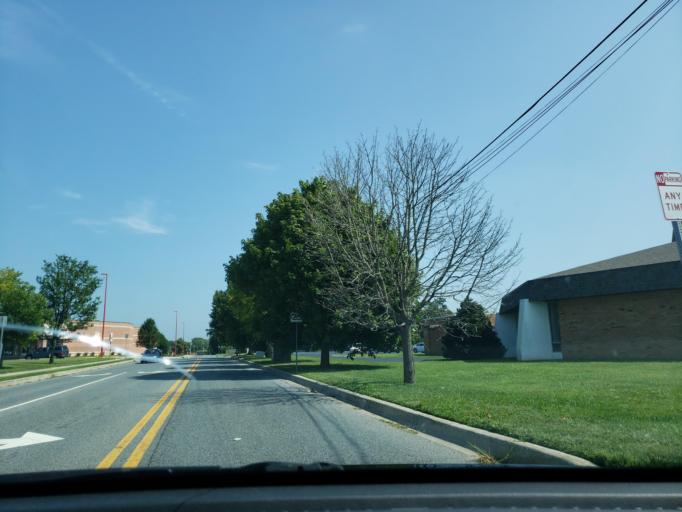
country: US
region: Delaware
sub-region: Kent County
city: Dover
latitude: 39.1575
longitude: -75.5082
